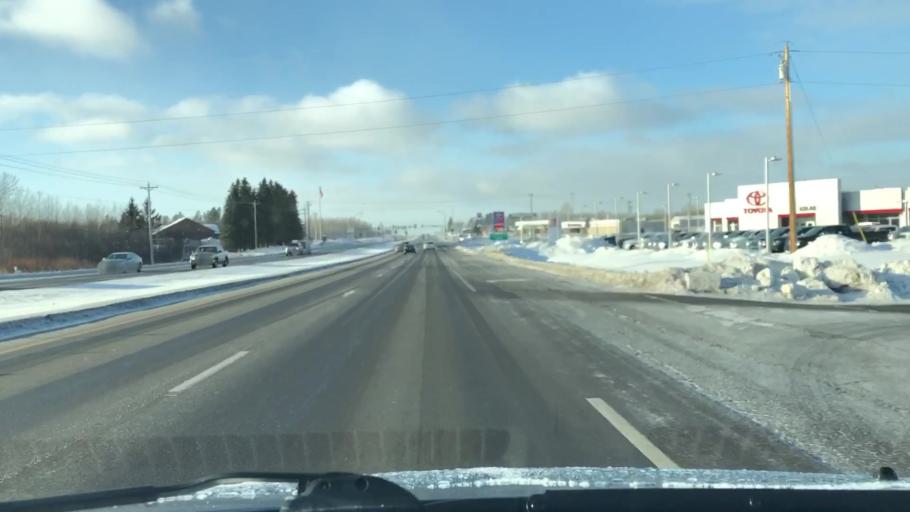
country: US
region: Minnesota
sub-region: Saint Louis County
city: Hermantown
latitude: 46.8201
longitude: -92.1833
